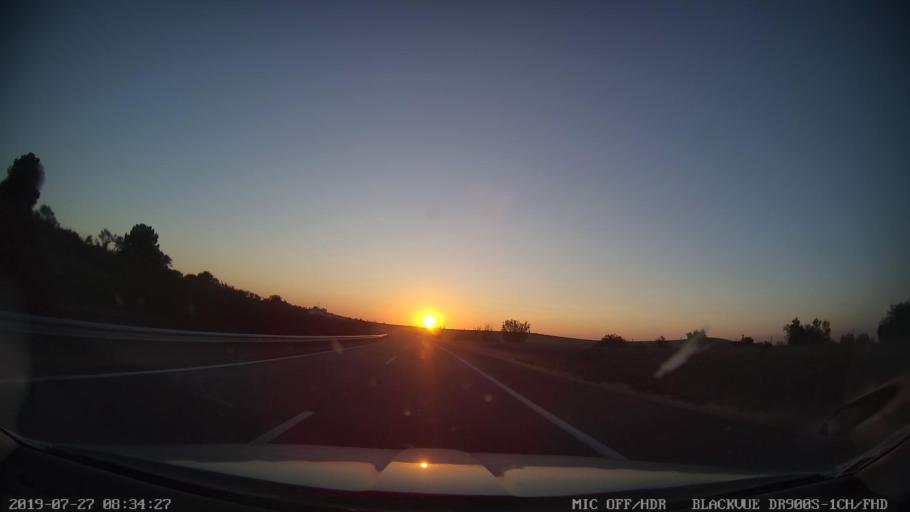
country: ES
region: Extremadura
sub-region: Provincia de Badajoz
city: Talavera La Real
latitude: 38.8656
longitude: -6.7958
